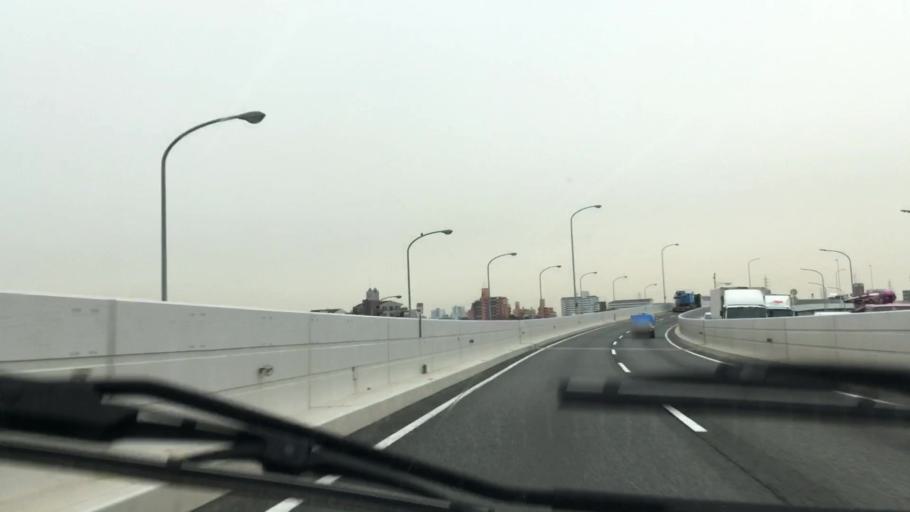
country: JP
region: Aichi
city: Chiryu
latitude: 34.9881
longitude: 137.0397
